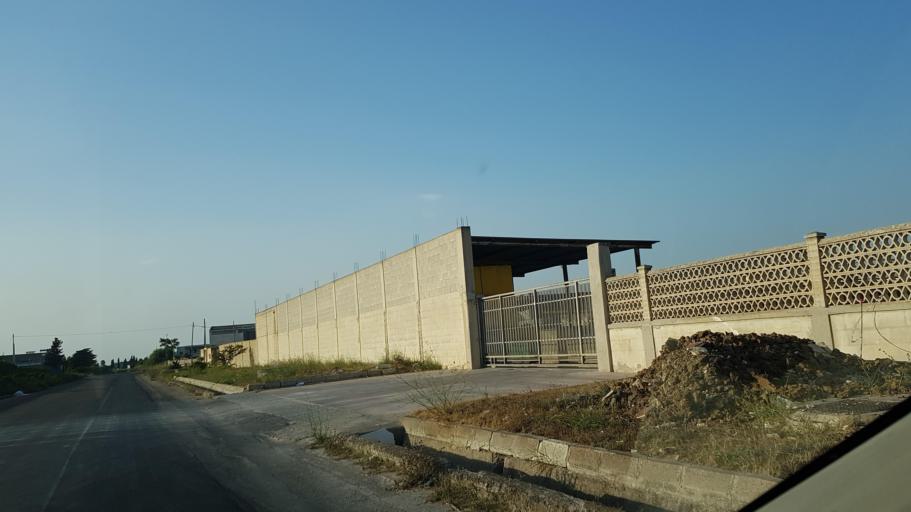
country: IT
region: Apulia
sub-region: Provincia di Brindisi
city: La Rosa
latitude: 40.6270
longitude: 17.9725
